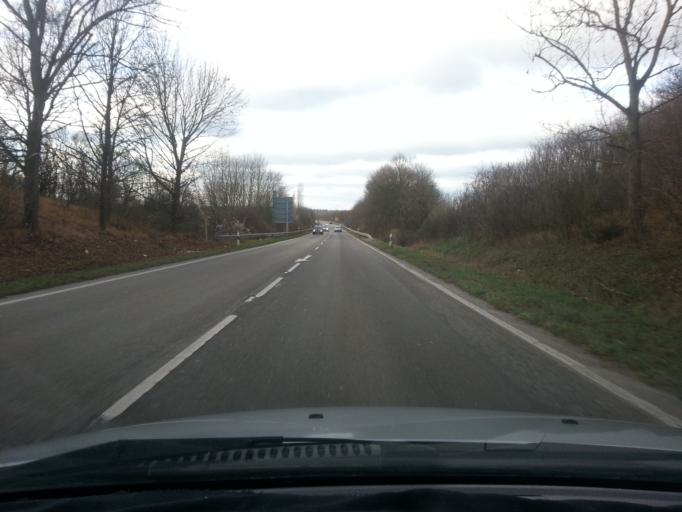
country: DE
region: Baden-Wuerttemberg
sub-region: Karlsruhe Region
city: Kronau
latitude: 49.2090
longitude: 8.6480
